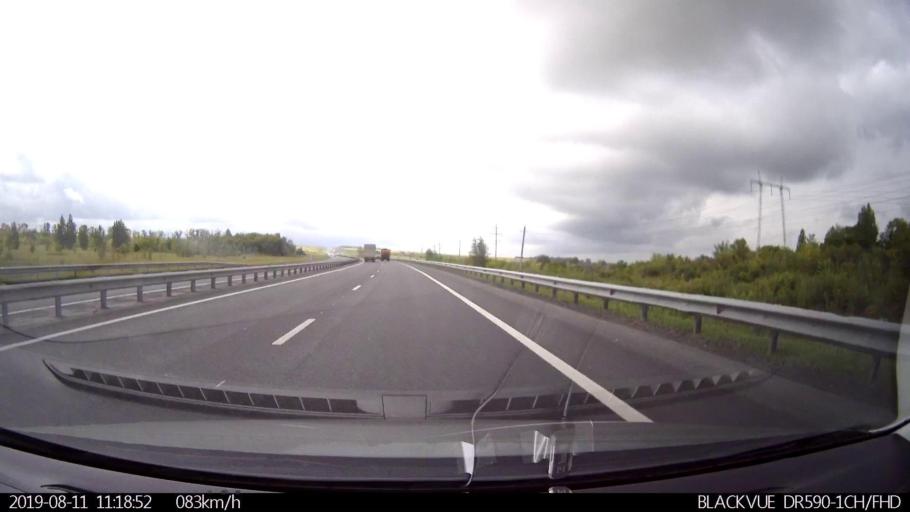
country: RU
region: Ulyanovsk
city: Novoul'yanovsk
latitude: 54.1757
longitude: 48.2652
